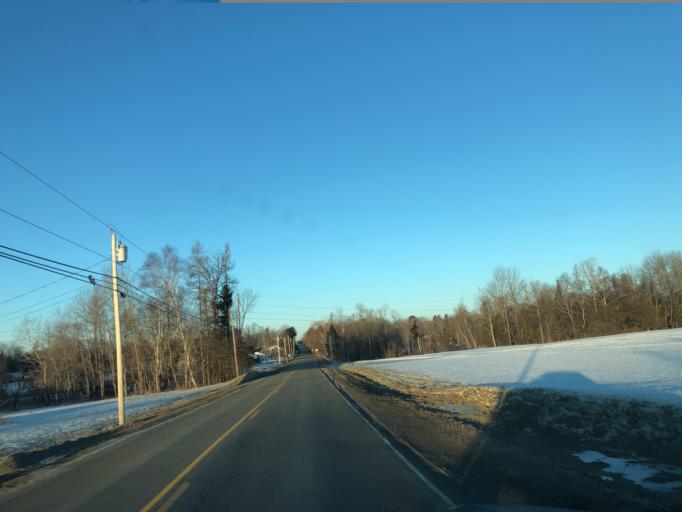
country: US
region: Maine
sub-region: Penobscot County
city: Charleston
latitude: 45.0069
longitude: -69.0148
